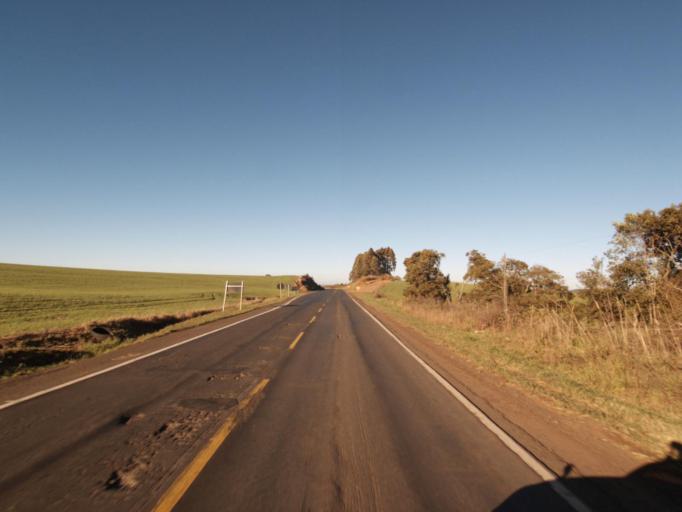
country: AR
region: Misiones
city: Bernardo de Irigoyen
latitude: -26.3174
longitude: -53.5495
